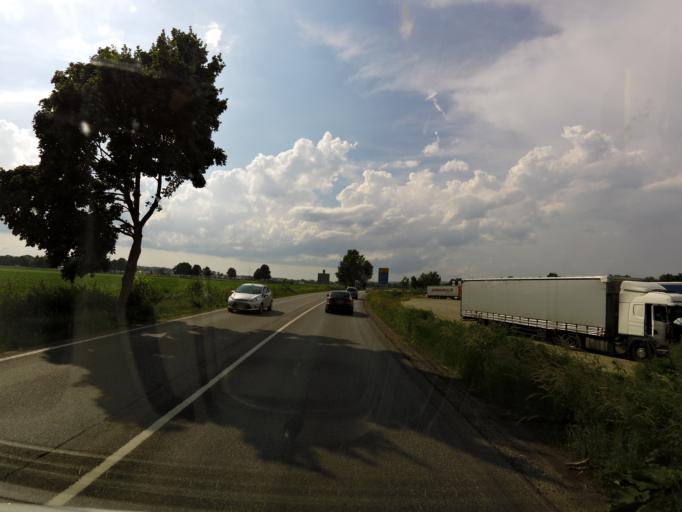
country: DE
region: Bavaria
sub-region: Lower Bavaria
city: Hengersberg
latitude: 48.7664
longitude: 13.0437
